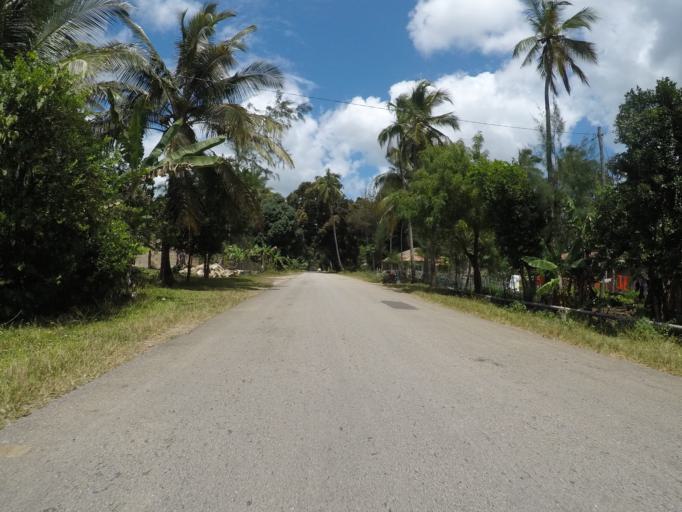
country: TZ
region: Zanzibar Central/South
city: Nganane
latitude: -6.3000
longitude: 39.4337
